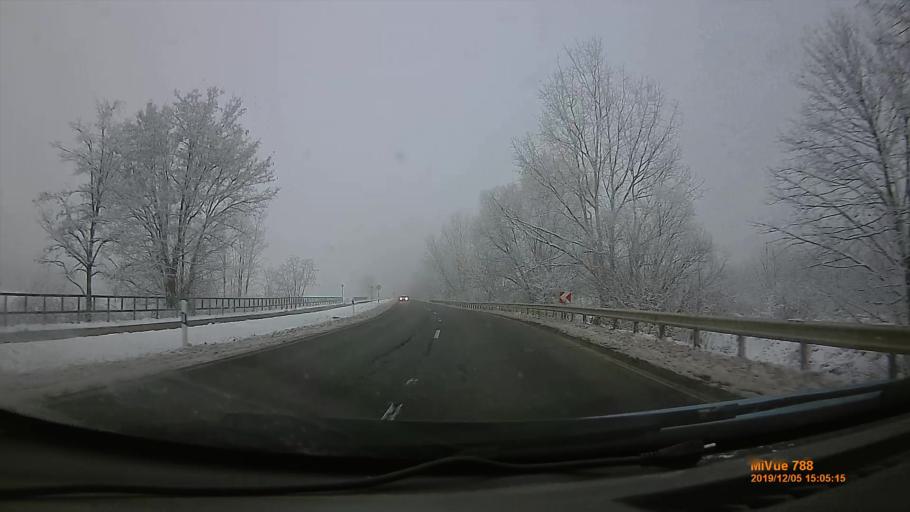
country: HU
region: Szabolcs-Szatmar-Bereg
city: Tiszanagyfalu
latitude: 48.1077
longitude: 21.4889
